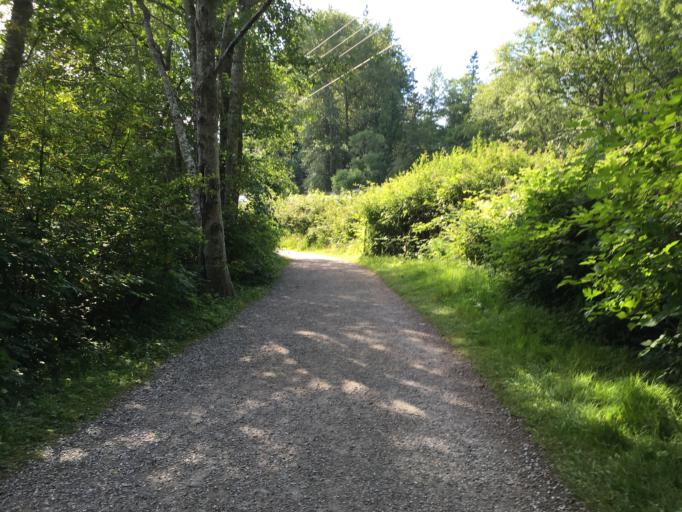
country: US
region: Washington
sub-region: Whatcom County
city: Geneva
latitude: 48.7062
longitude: -122.4513
